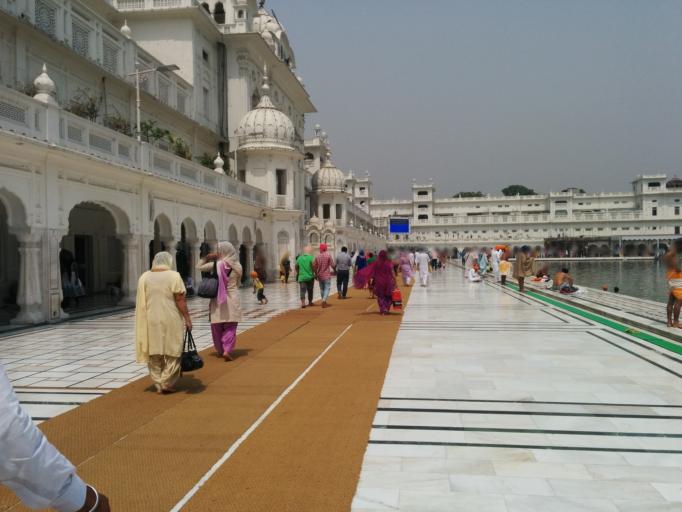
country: IN
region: Punjab
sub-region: Amritsar
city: Amritsar
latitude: 31.6191
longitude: 74.8764
